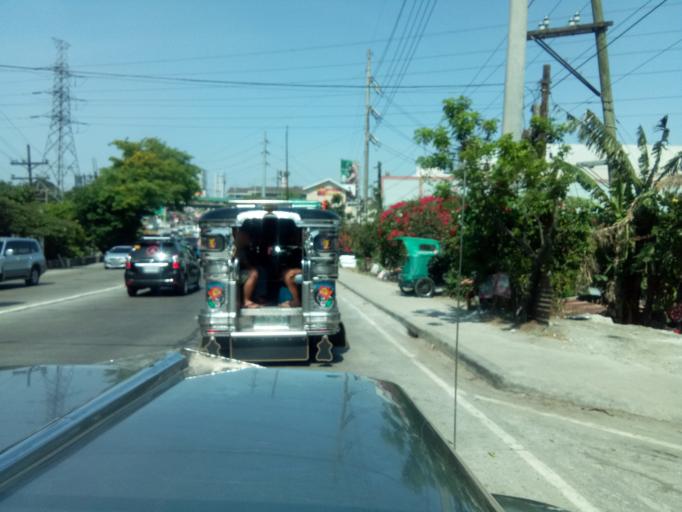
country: PH
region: Calabarzon
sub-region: Province of Cavite
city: Dasmarinas
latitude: 14.2999
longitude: 120.9516
